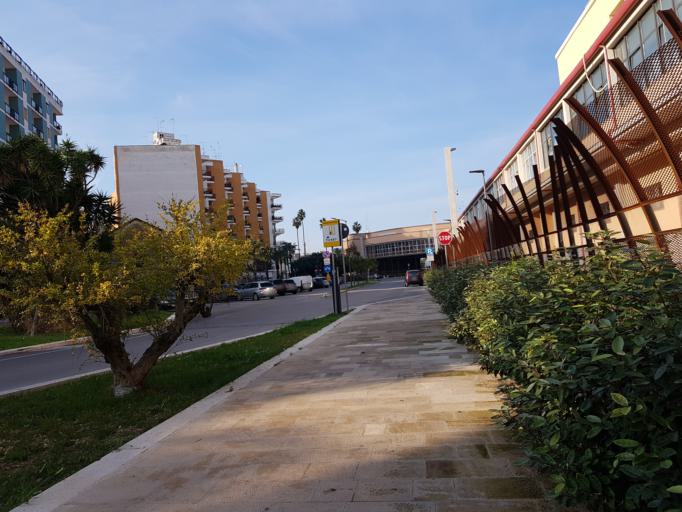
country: IT
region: Apulia
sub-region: Provincia di Brindisi
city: Brindisi
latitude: 40.6383
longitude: 17.9492
